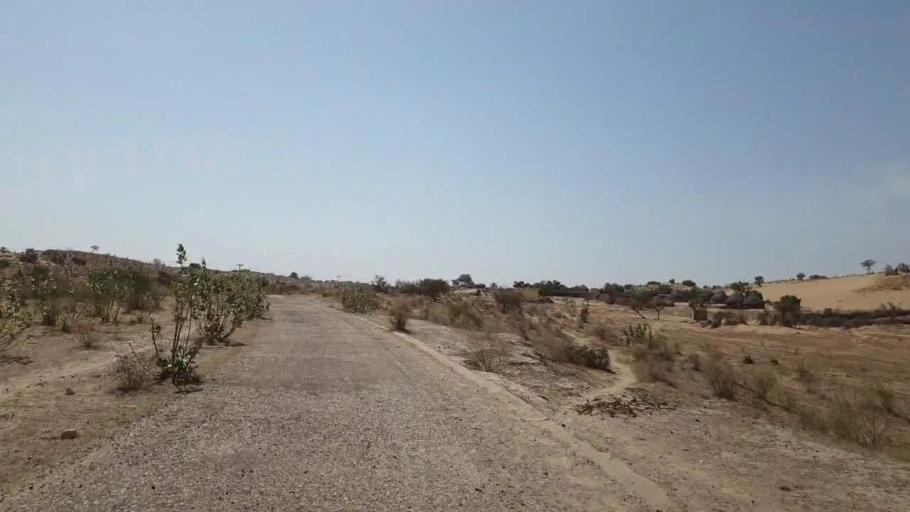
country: PK
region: Sindh
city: Umarkot
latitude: 25.2178
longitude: 69.9386
